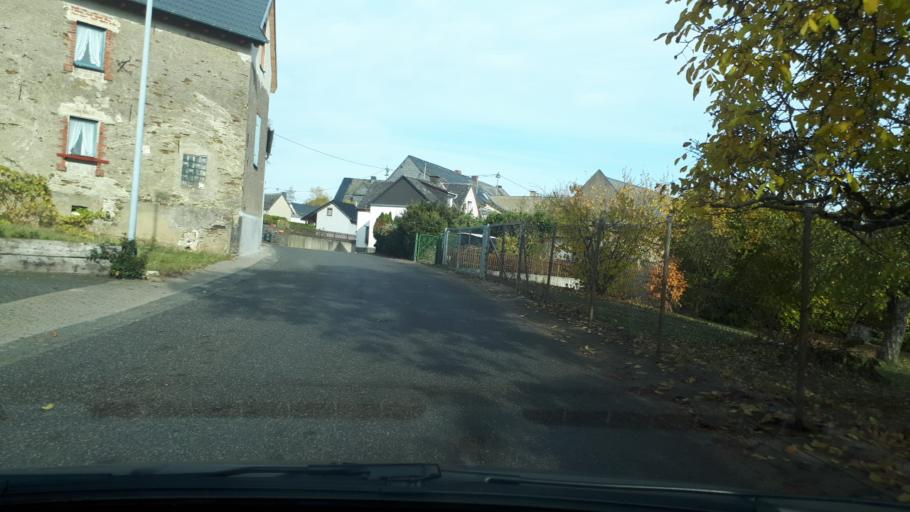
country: DE
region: Rheinland-Pfalz
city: Landkern
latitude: 50.1925
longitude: 7.1500
